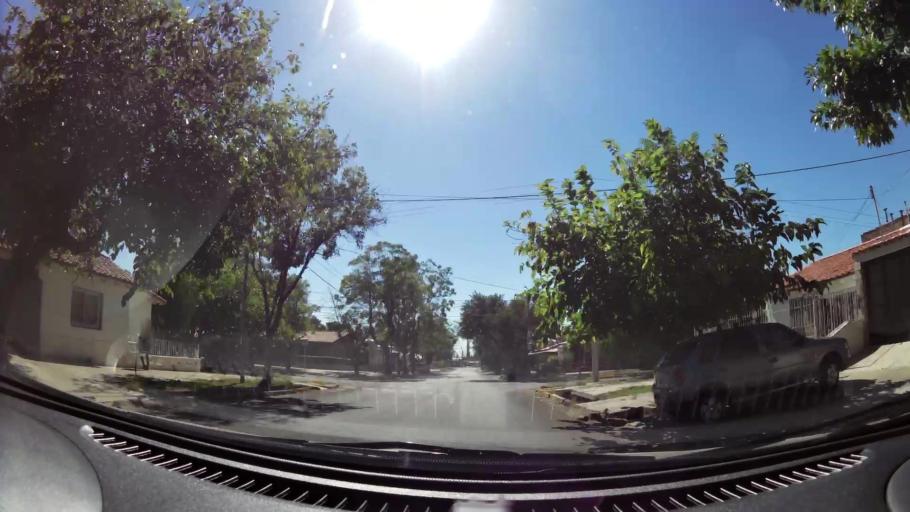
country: AR
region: Mendoza
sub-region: Departamento de Godoy Cruz
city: Godoy Cruz
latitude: -32.9158
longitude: -68.8708
